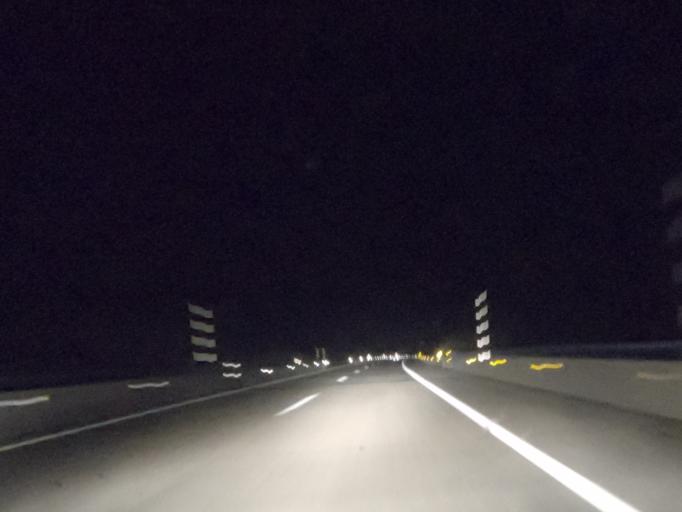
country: ES
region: Castille and Leon
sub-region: Provincia de Zamora
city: Vega de Tera
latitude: 42.0090
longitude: -6.1131
